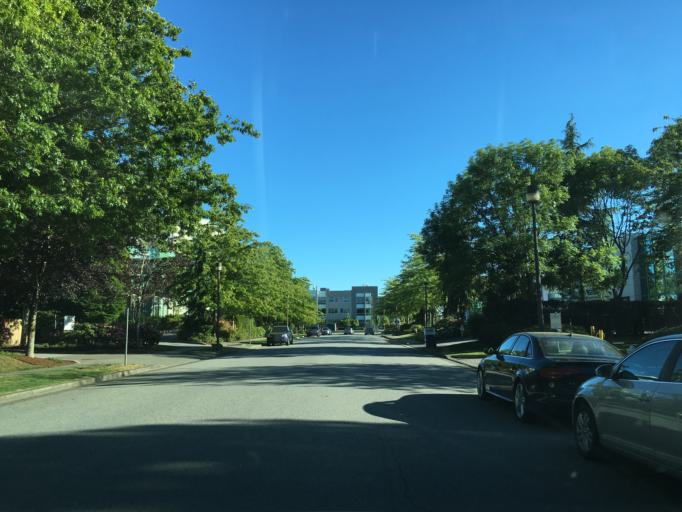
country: CA
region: British Columbia
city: Richmond
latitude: 49.1733
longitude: -123.0717
